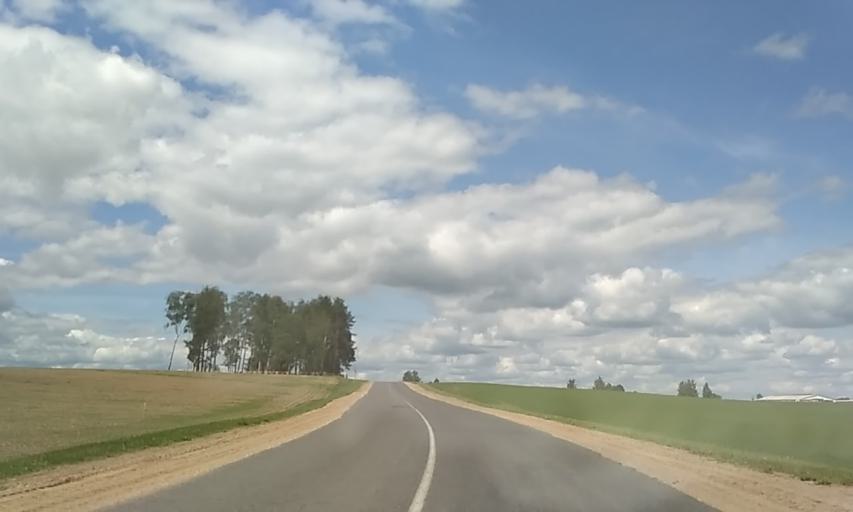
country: BY
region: Minsk
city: Krupki
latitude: 54.3415
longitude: 29.1044
